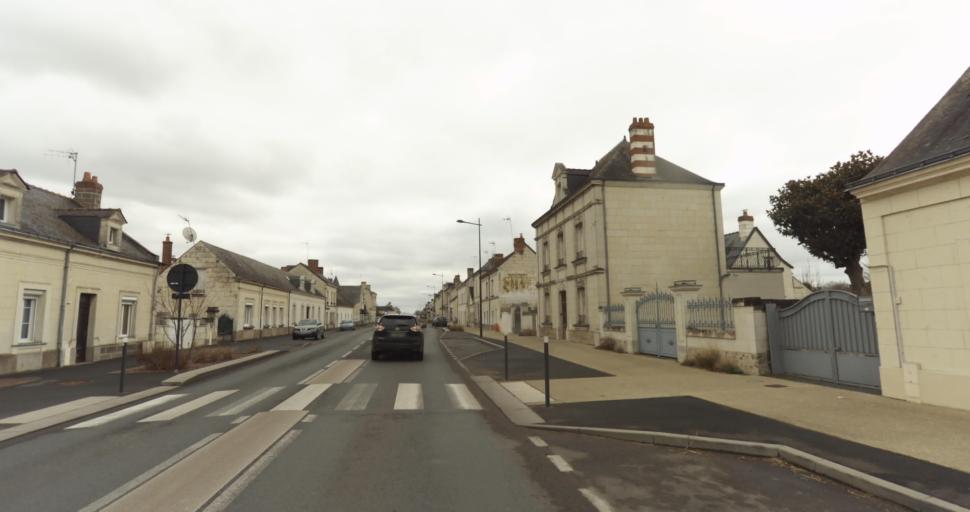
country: FR
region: Pays de la Loire
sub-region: Departement de Maine-et-Loire
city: Vivy
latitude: 47.3273
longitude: -0.0573
